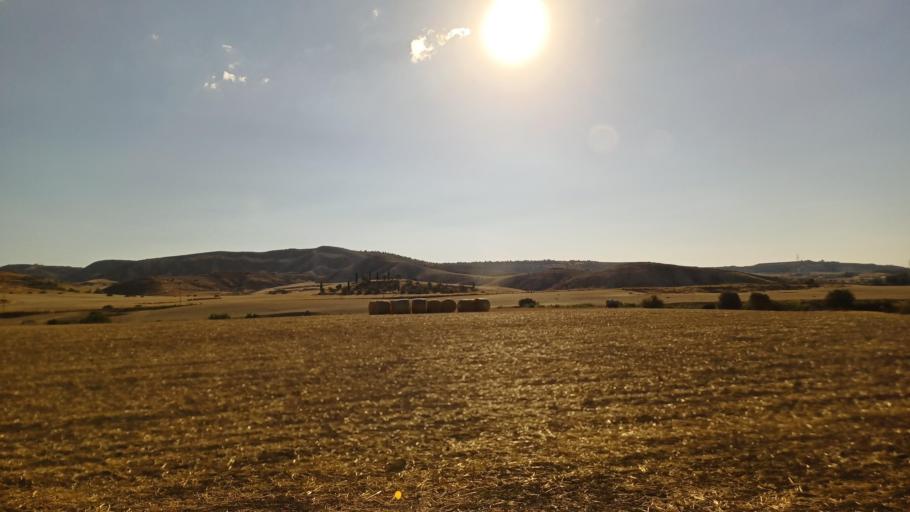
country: CY
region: Larnaka
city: Voroklini
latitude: 35.0098
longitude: 33.6383
